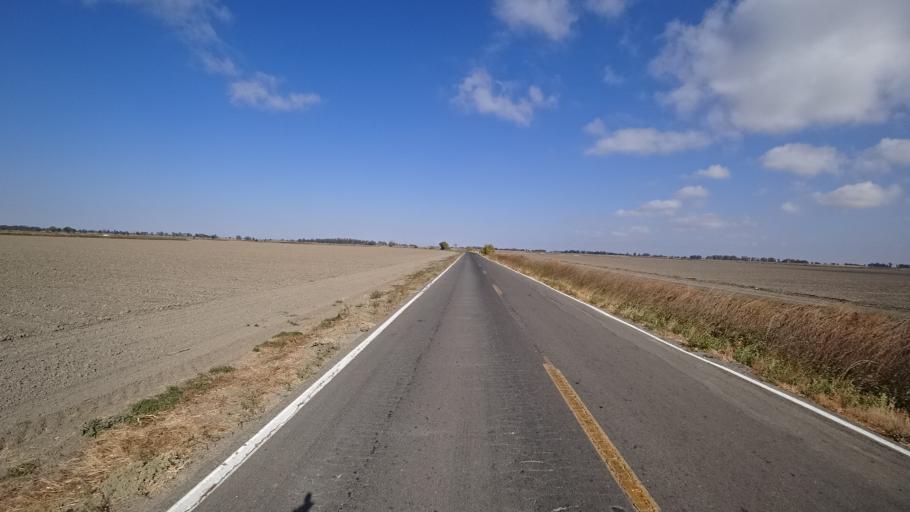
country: US
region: California
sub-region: Yolo County
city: Woodland
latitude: 38.8397
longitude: -121.7519
